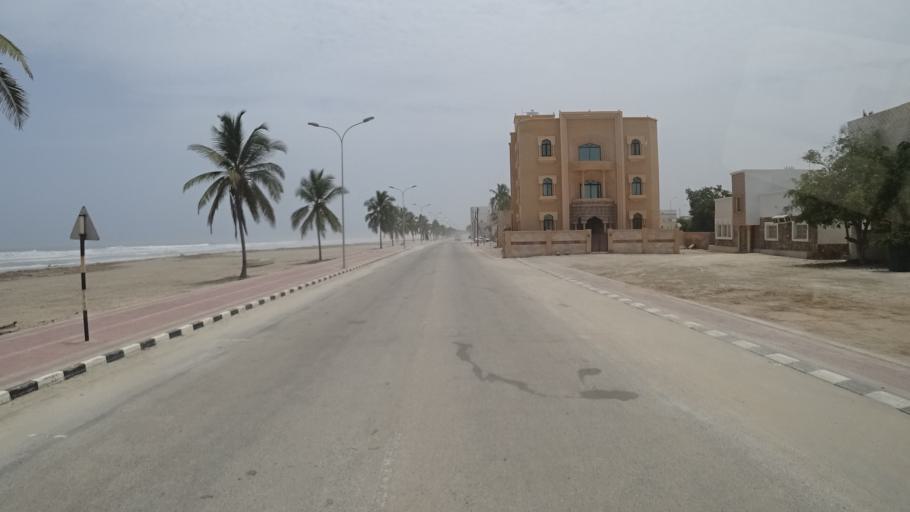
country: OM
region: Zufar
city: Salalah
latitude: 17.0344
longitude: 54.4000
